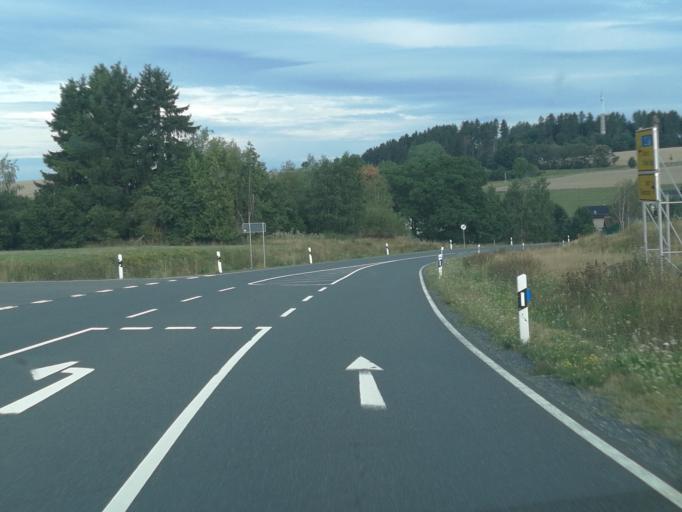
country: DE
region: Bavaria
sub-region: Upper Franconia
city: Regnitzlosau
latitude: 50.3351
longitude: 12.0829
